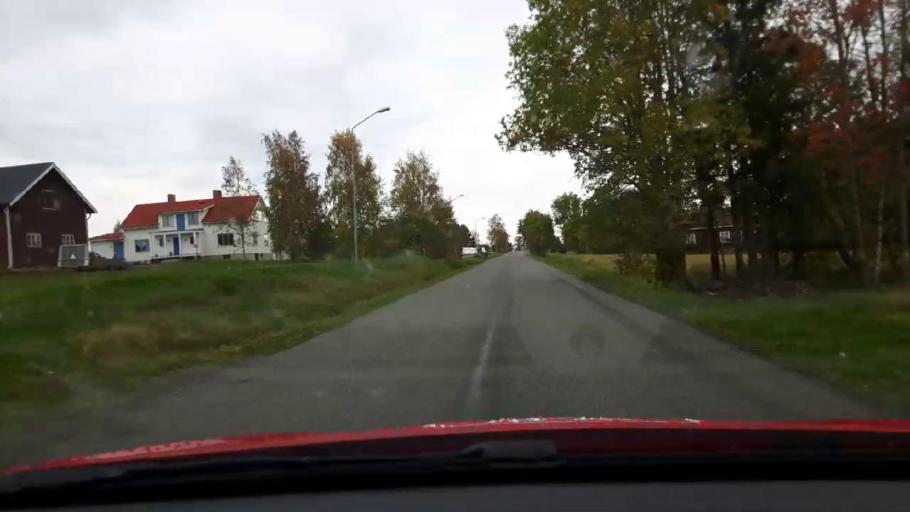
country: SE
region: Jaemtland
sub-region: Bergs Kommun
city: Hoverberg
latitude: 62.9623
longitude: 14.4898
